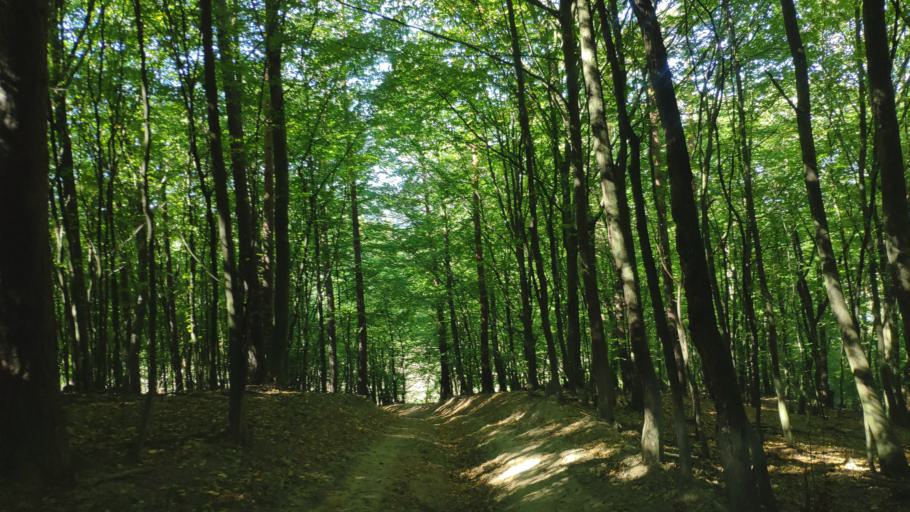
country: SK
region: Presovsky
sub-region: Okres Presov
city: Presov
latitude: 48.9795
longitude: 21.1416
